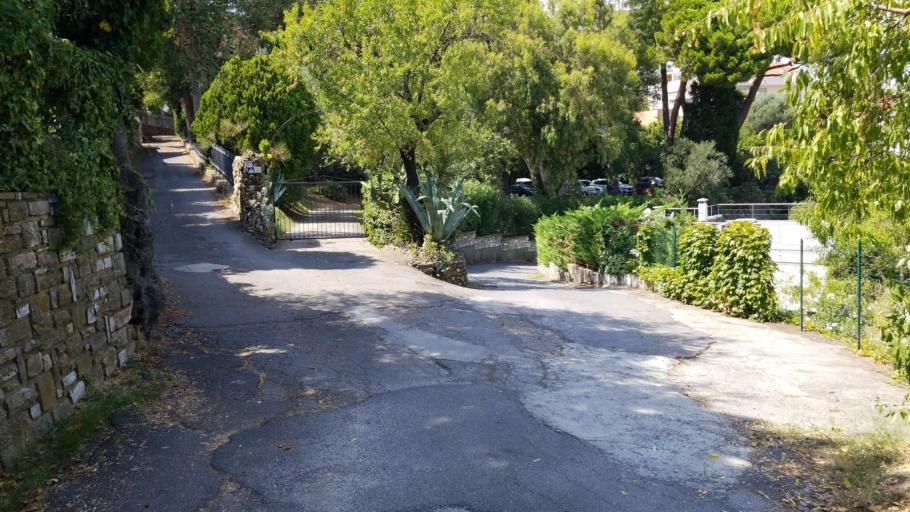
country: IT
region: Liguria
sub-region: Provincia di Imperia
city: Diano Marina
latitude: 43.8992
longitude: 8.0710
